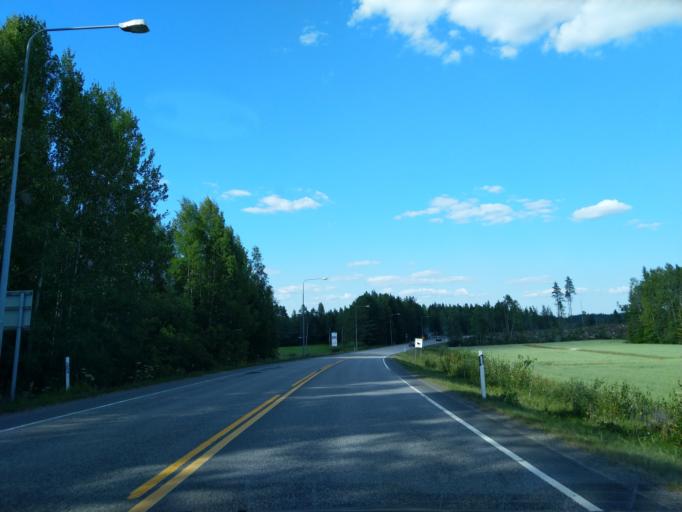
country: FI
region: Pirkanmaa
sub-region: Luoteis-Pirkanmaa
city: Kihnioe
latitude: 62.1957
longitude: 23.1724
